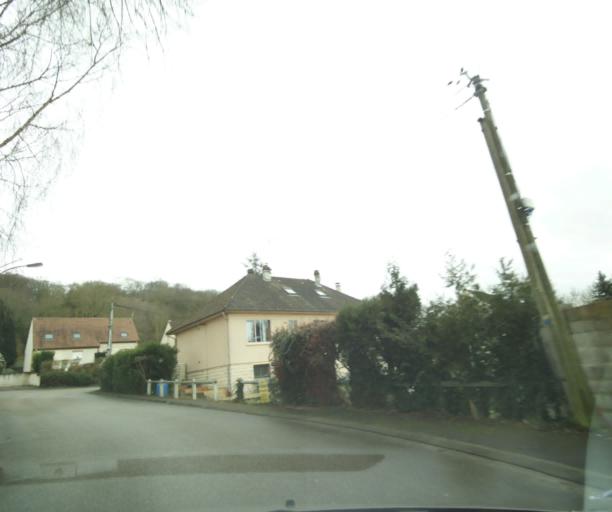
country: FR
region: Picardie
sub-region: Departement de l'Oise
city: Noyon
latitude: 49.5900
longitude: 3.0183
